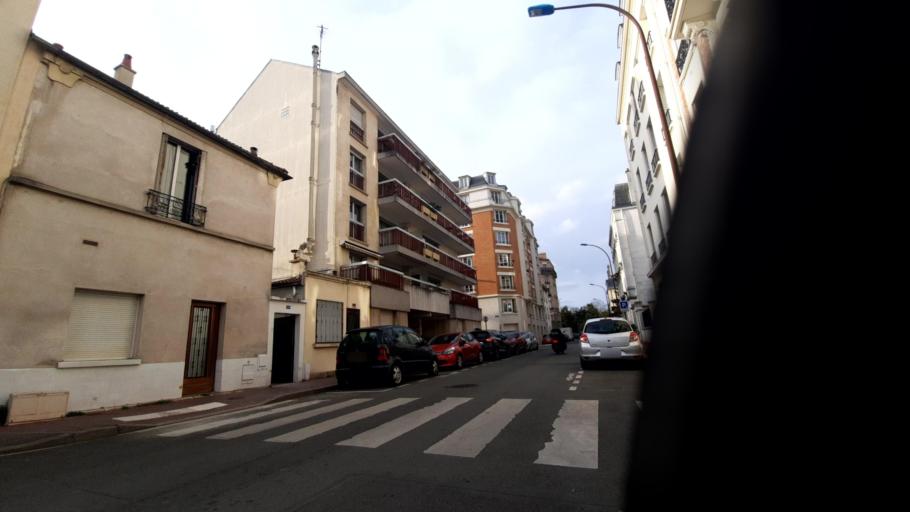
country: FR
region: Ile-de-France
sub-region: Departement du Val-de-Marne
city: Charenton-le-Pont
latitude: 48.8238
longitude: 2.4158
